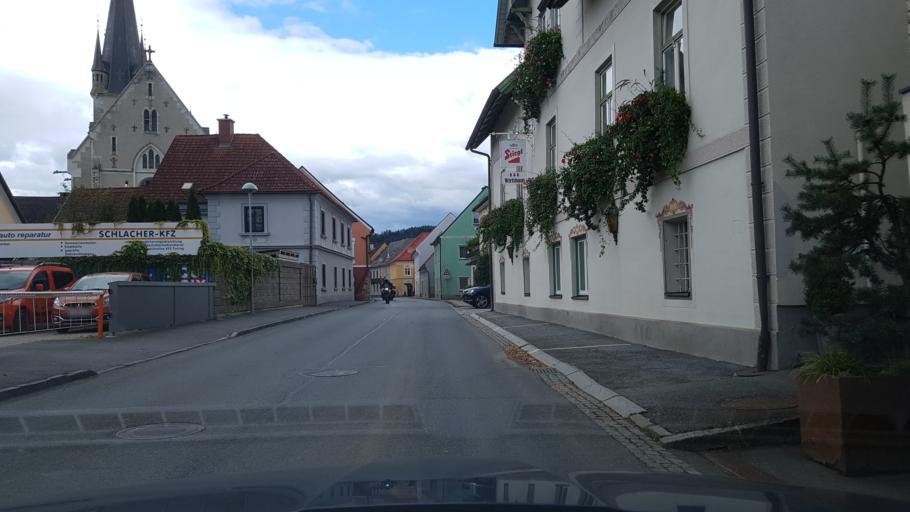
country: AT
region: Styria
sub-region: Politischer Bezirk Murtal
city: Weisskirchen in Steiermark
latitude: 47.1541
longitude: 14.7366
